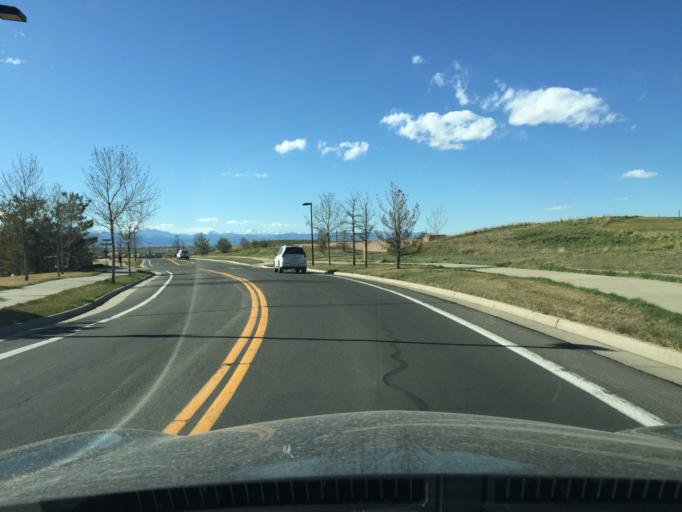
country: US
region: Colorado
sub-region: Boulder County
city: Erie
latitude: 40.0134
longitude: -105.0339
